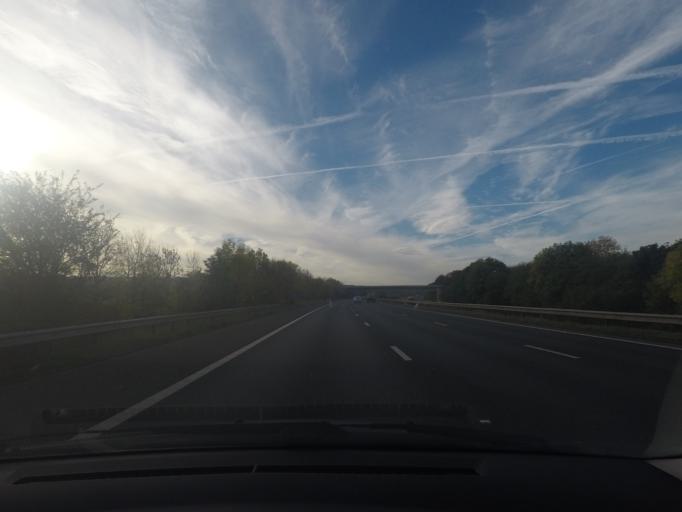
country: GB
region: England
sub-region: City and Borough of Wakefield
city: Crigglestone
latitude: 53.6314
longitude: -1.5399
